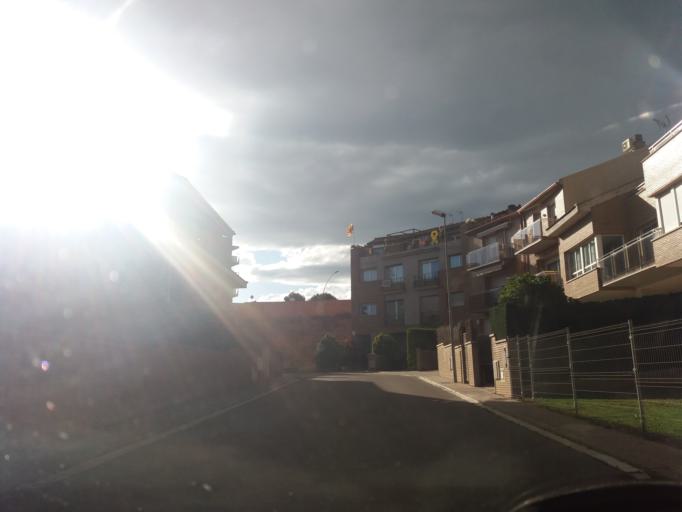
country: ES
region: Catalonia
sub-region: Provincia de Barcelona
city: Manresa
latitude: 41.7433
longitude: 1.8359
